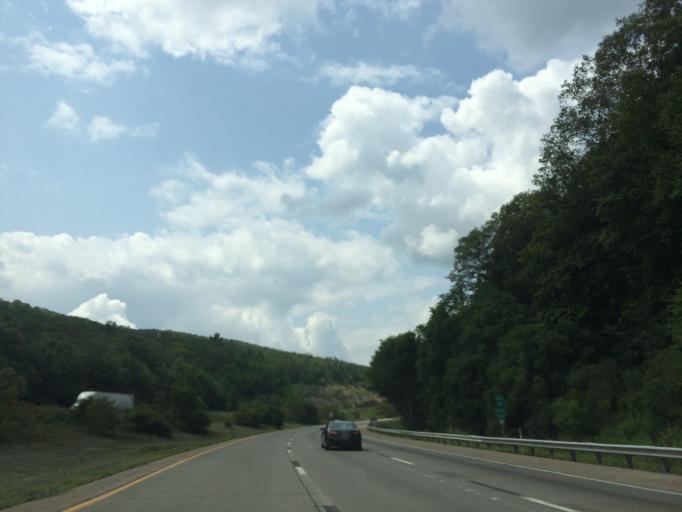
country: US
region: Pennsylvania
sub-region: Luzerne County
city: Ashley
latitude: 41.1869
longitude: -75.9195
